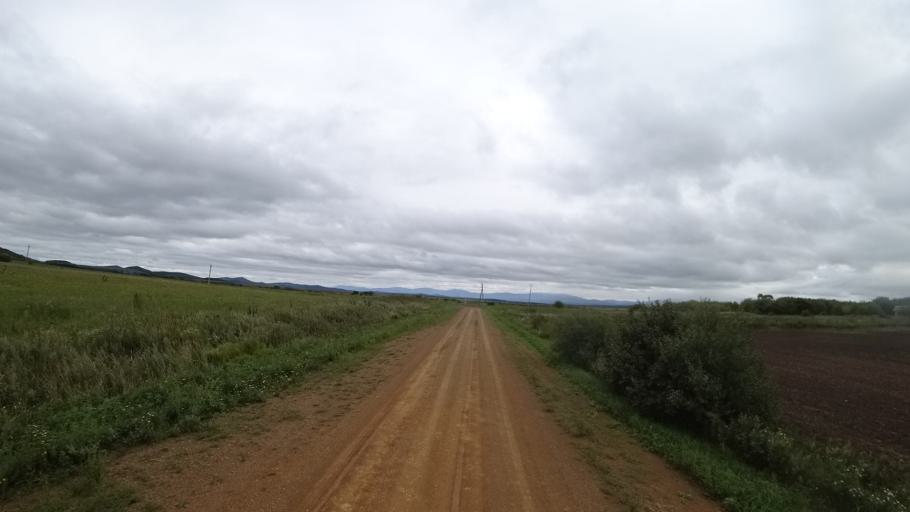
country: RU
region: Primorskiy
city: Chernigovka
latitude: 44.4353
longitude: 132.5907
